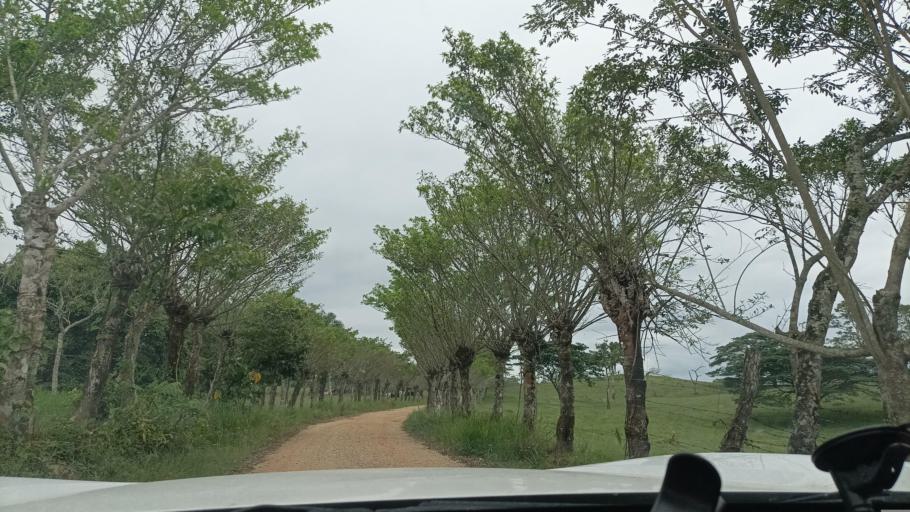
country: MX
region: Veracruz
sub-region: Uxpanapa
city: Poblado Cinco
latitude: 17.5043
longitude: -94.5626
